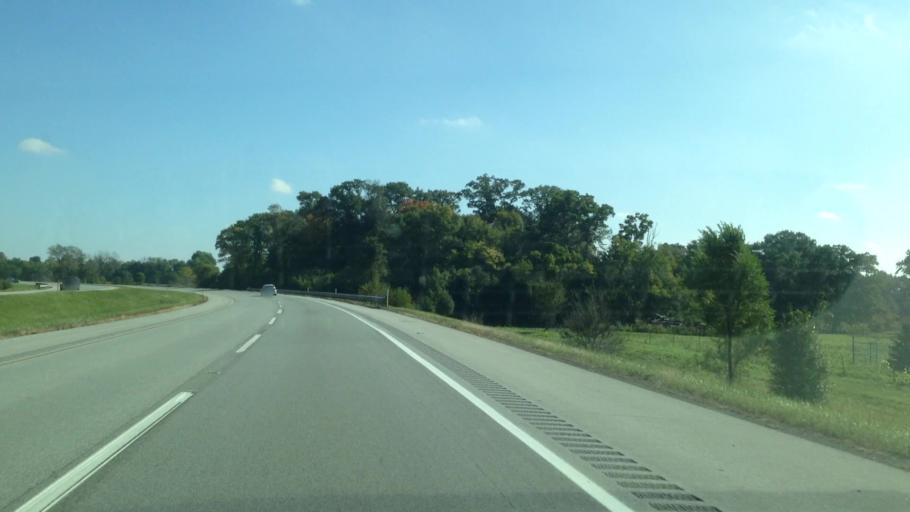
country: US
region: Indiana
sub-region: LaPorte County
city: LaPorte
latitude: 41.6736
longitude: -86.6777
